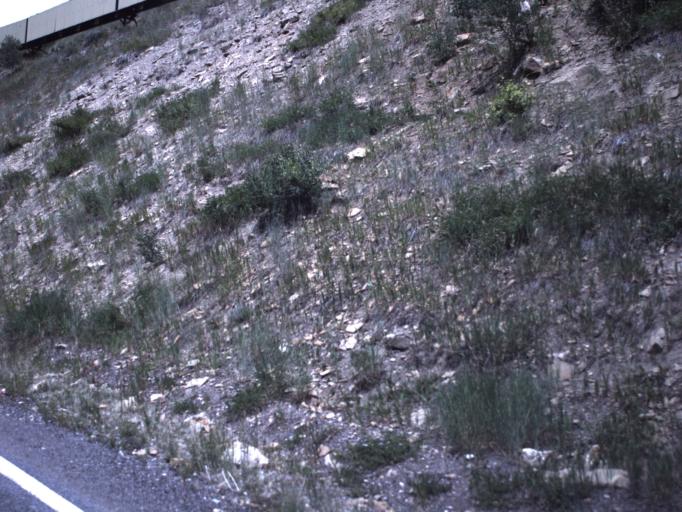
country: US
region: Utah
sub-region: Sanpete County
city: Fairview
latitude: 39.6824
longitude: -111.1897
